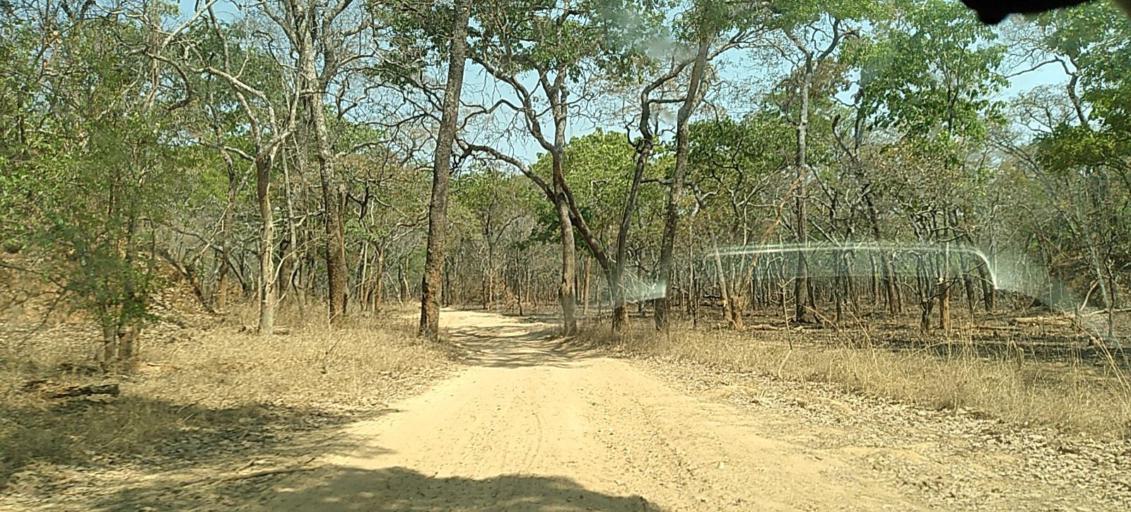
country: ZM
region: North-Western
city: Kasempa
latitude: -13.3926
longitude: 25.6215
